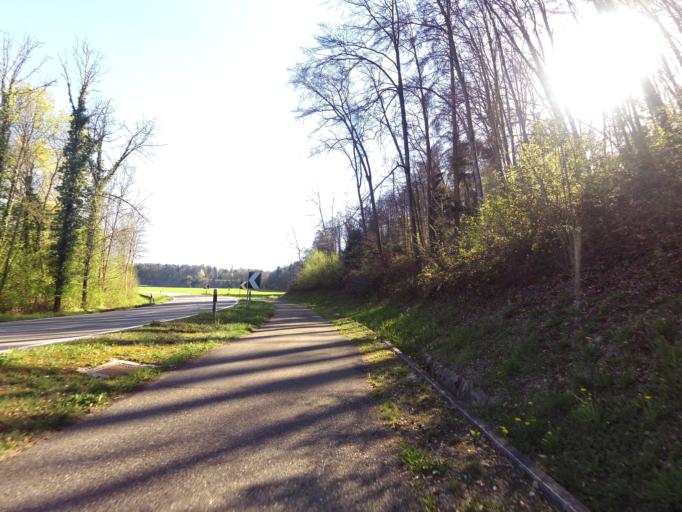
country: CH
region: Aargau
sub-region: Bezirk Zurzach
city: Koblenz
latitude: 47.5945
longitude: 8.2146
